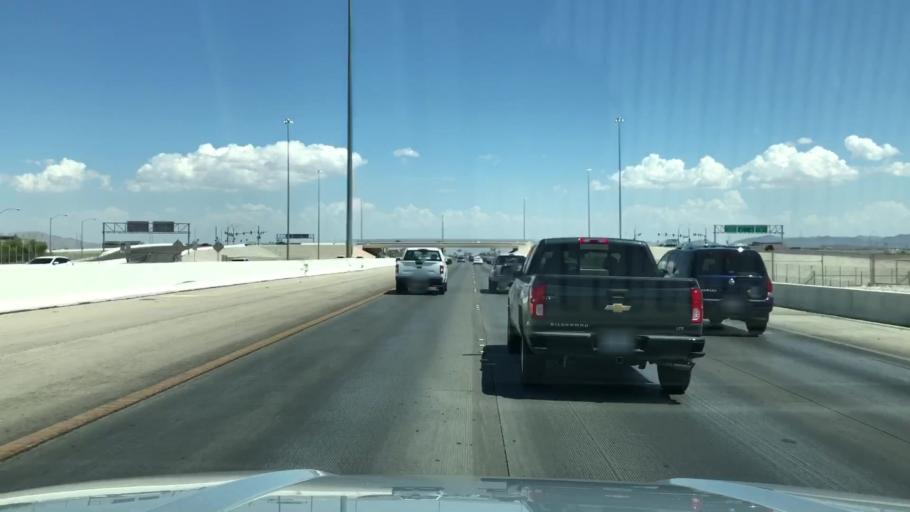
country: US
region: Nevada
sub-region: Clark County
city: Spring Valley
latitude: 36.0660
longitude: -115.2654
